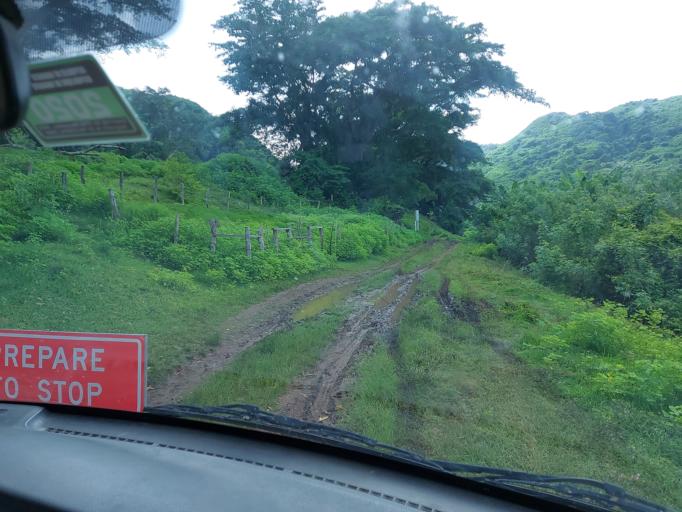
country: VU
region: Tafea
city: Isangel
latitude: -18.8199
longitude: 169.0225
